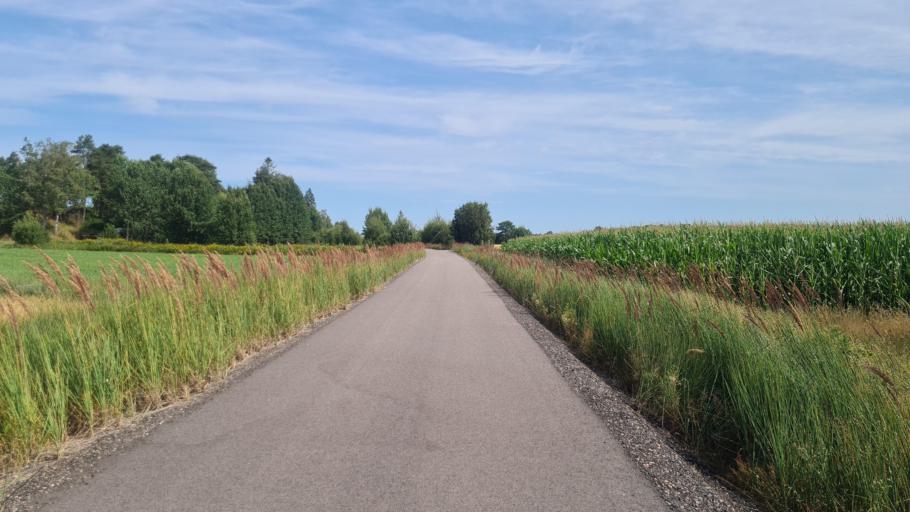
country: SE
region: Kronoberg
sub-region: Ljungby Kommun
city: Lagan
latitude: 56.8967
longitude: 13.9873
